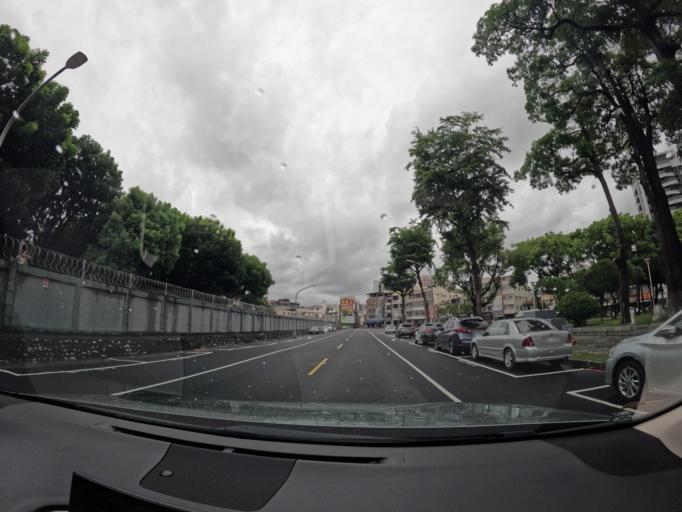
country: TW
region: Taiwan
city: Fengshan
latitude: 22.6219
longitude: 120.3681
